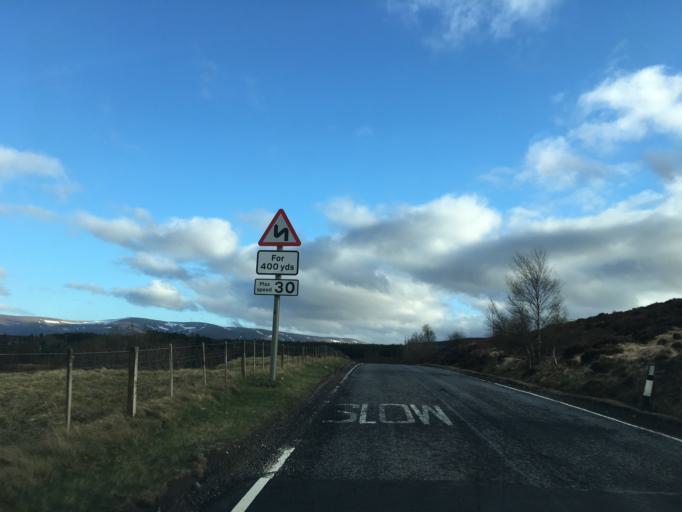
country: GB
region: Scotland
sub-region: Highland
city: Kingussie
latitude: 56.9926
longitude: -4.2497
